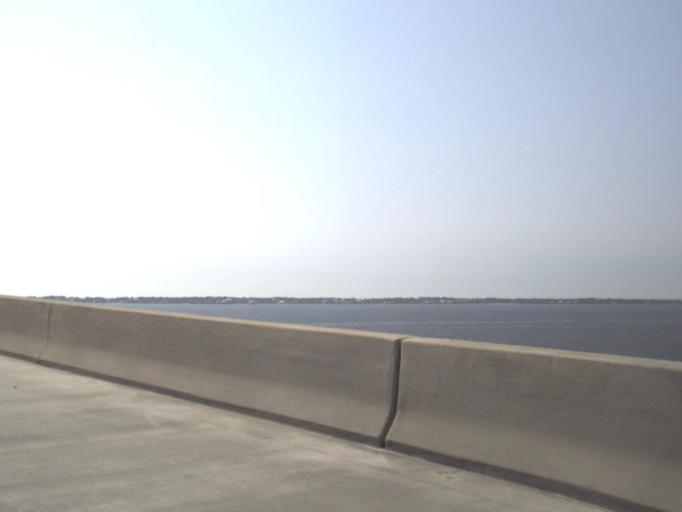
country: US
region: Florida
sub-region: Franklin County
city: Eastpoint
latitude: 29.6863
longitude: -84.8829
